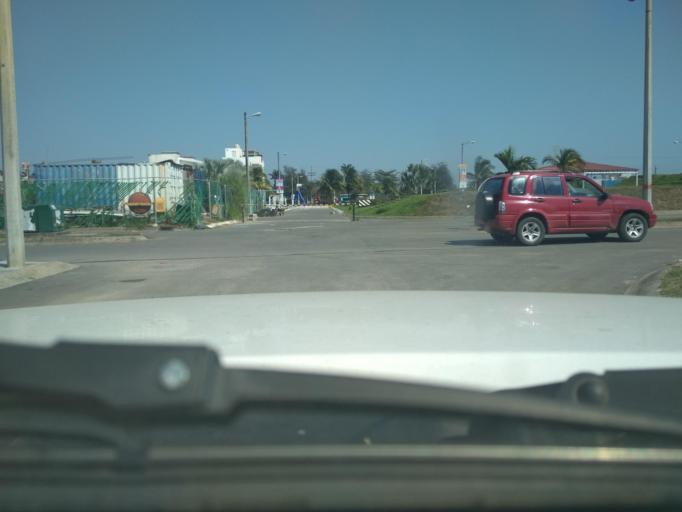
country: MX
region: Veracruz
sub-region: Veracruz
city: Las Amapolas
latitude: 19.1586
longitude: -96.2233
